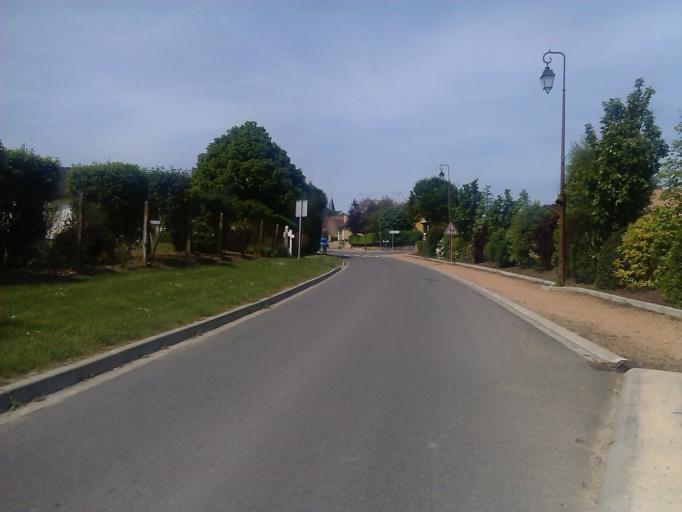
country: FR
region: Centre
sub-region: Departement du Cher
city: Saint-Amand-Montrond
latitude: 46.5994
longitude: 2.4995
